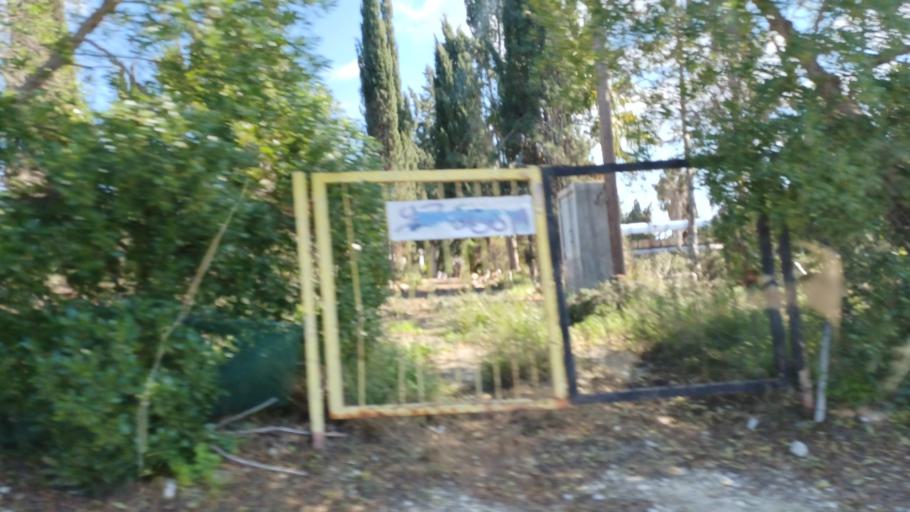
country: CY
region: Pafos
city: Paphos
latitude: 34.7485
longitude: 32.4374
